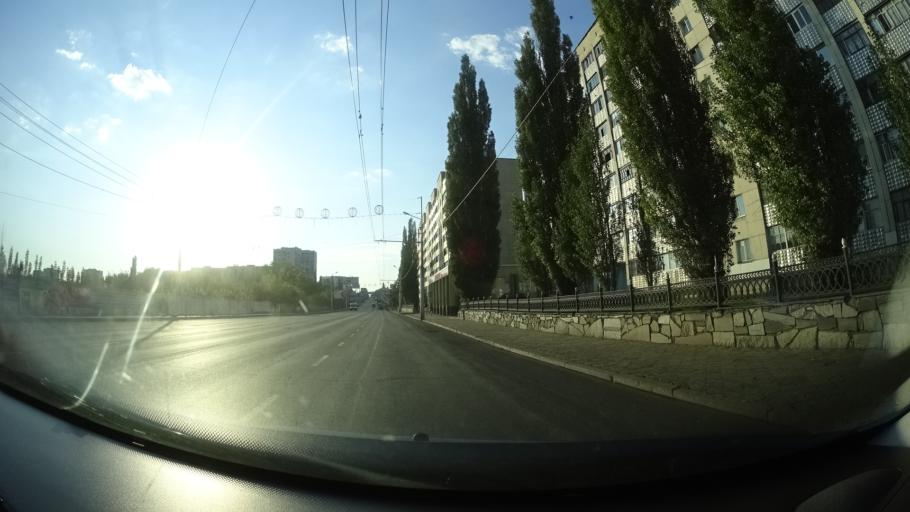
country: RU
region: Bashkortostan
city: Sterlitamak
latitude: 53.6212
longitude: 55.9570
